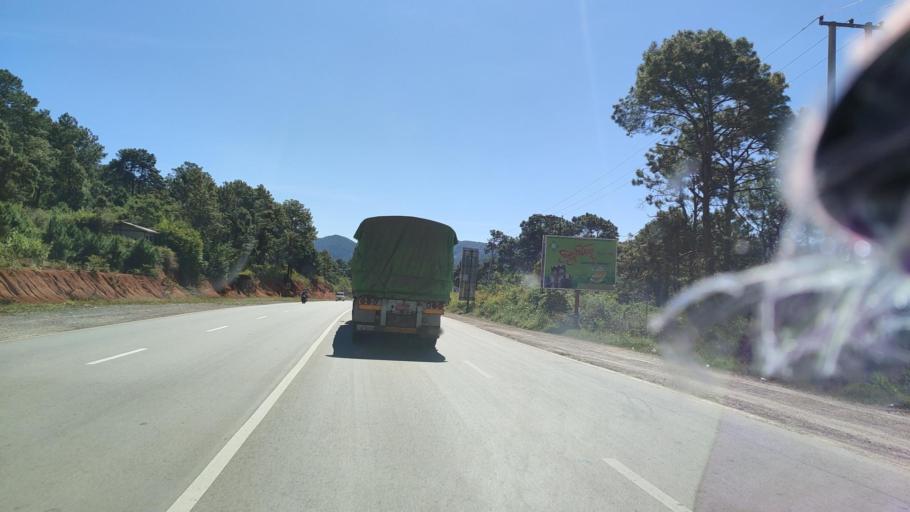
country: MM
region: Shan
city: Taunggyi
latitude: 20.6510
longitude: 96.5916
